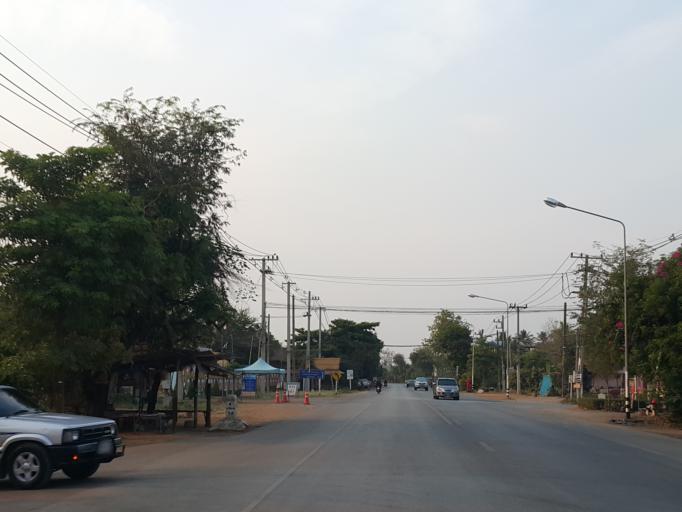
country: TH
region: Sukhothai
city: Sawankhalok
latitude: 17.2825
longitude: 99.8441
